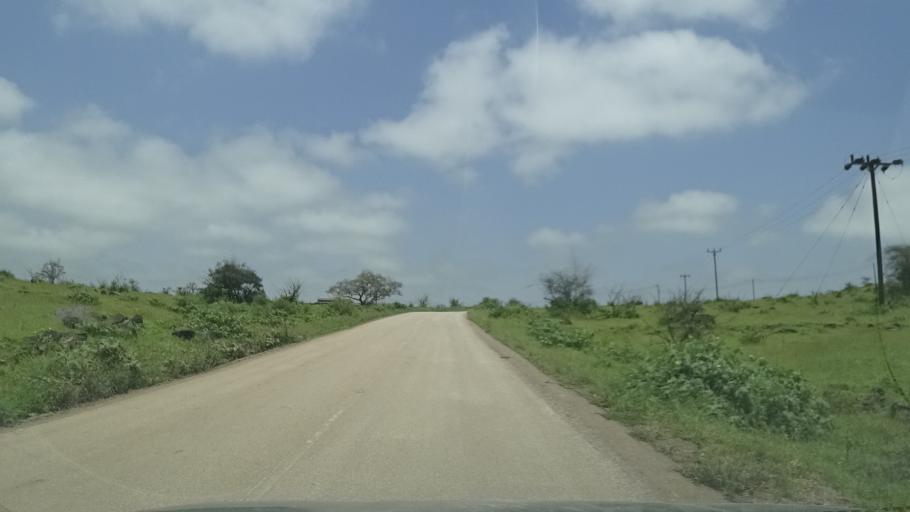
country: OM
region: Zufar
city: Salalah
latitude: 17.2064
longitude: 54.1903
